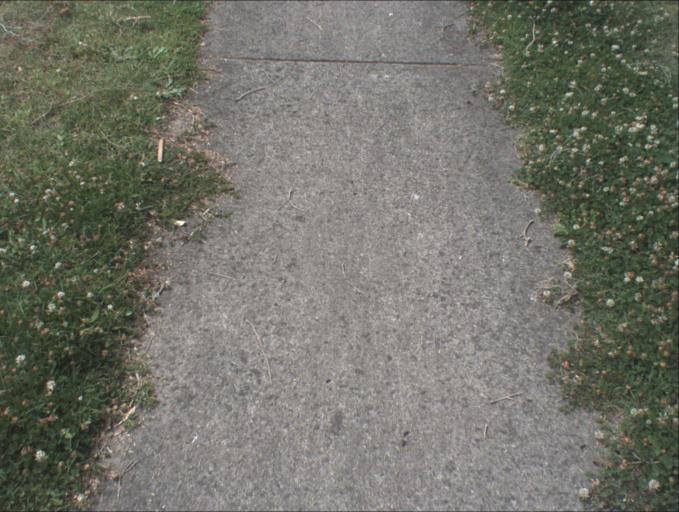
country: AU
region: Queensland
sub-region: Logan
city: Logan City
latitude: -27.6499
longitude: 153.1066
